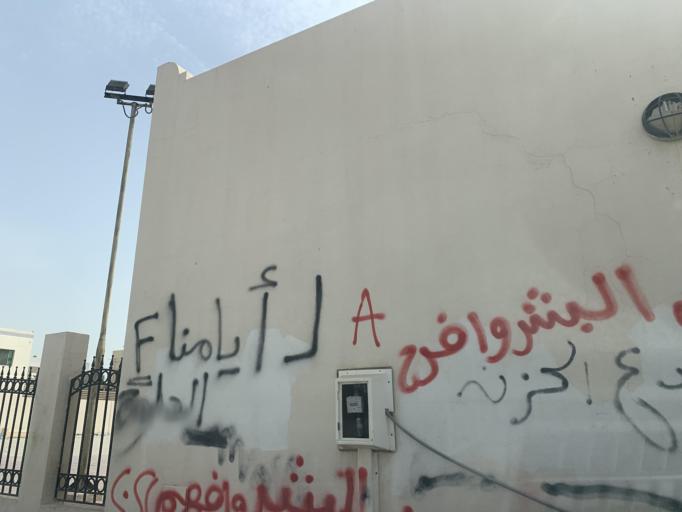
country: BH
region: Northern
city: Ar Rifa'
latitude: 26.1297
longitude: 50.5686
